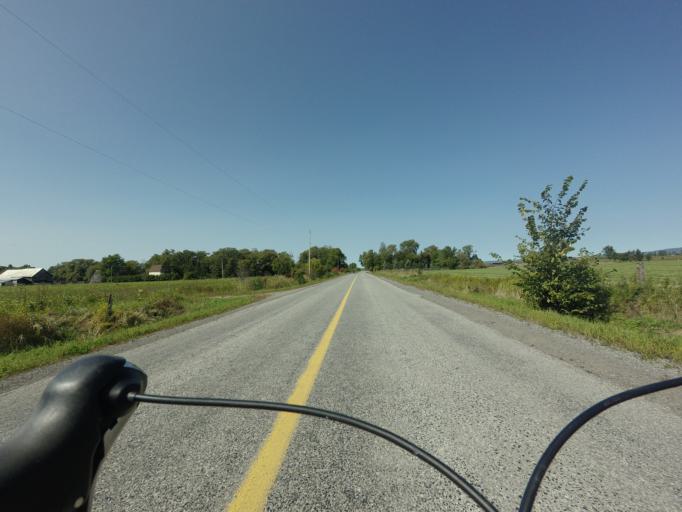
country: CA
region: Ontario
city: Bells Corners
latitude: 45.4384
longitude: -76.0680
